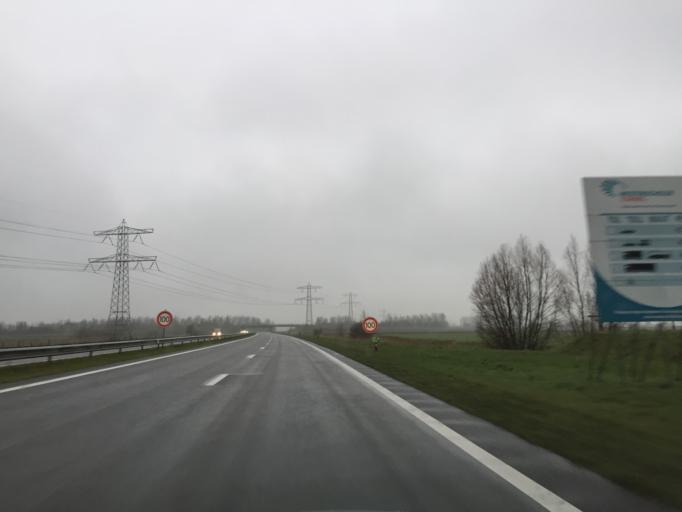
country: NL
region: Zeeland
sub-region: Gemeente Terneuzen
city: Terneuzen
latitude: 51.3107
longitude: 3.8006
